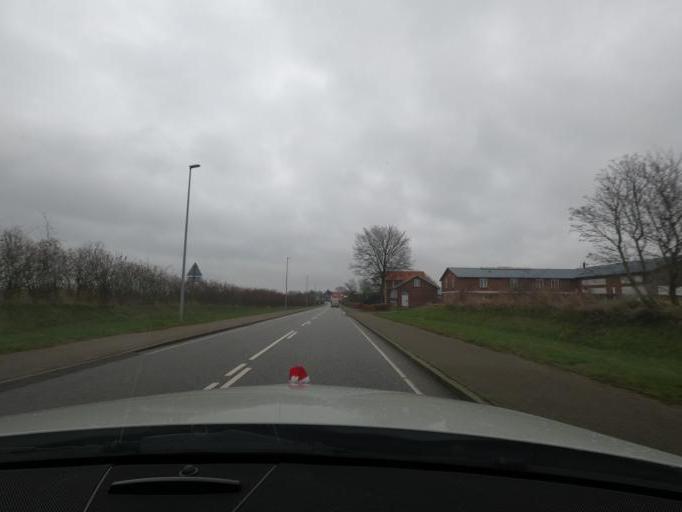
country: DK
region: South Denmark
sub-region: Haderslev Kommune
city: Starup
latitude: 55.2556
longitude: 9.6943
